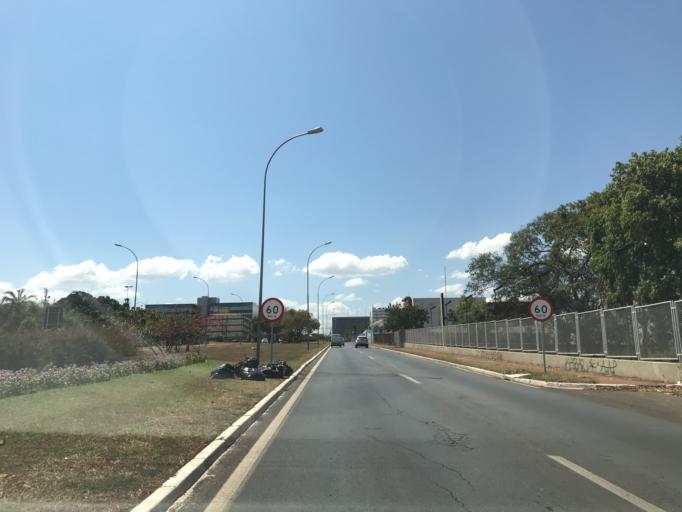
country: BR
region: Federal District
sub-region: Brasilia
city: Brasilia
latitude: -15.7932
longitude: -47.9119
